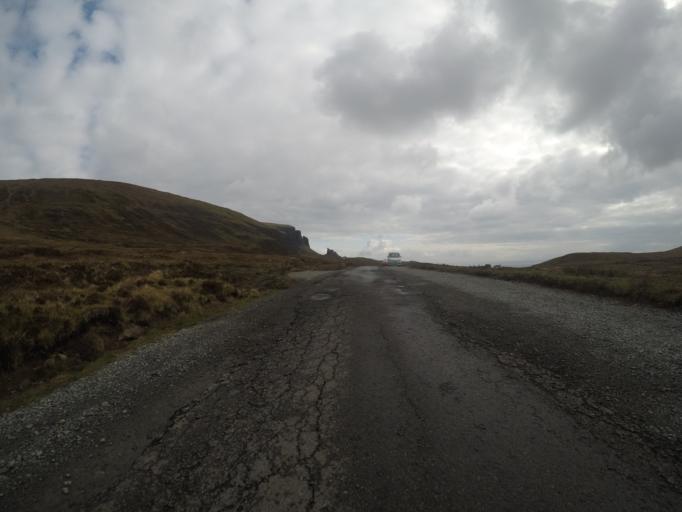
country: GB
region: Scotland
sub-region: Highland
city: Portree
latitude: 57.6279
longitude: -6.2938
